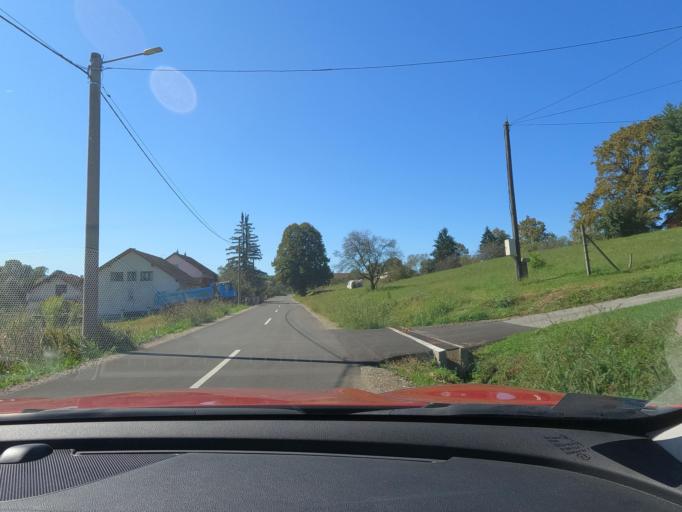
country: HR
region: Sisacko-Moslavacka
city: Petrinja
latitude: 45.4561
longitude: 16.2627
